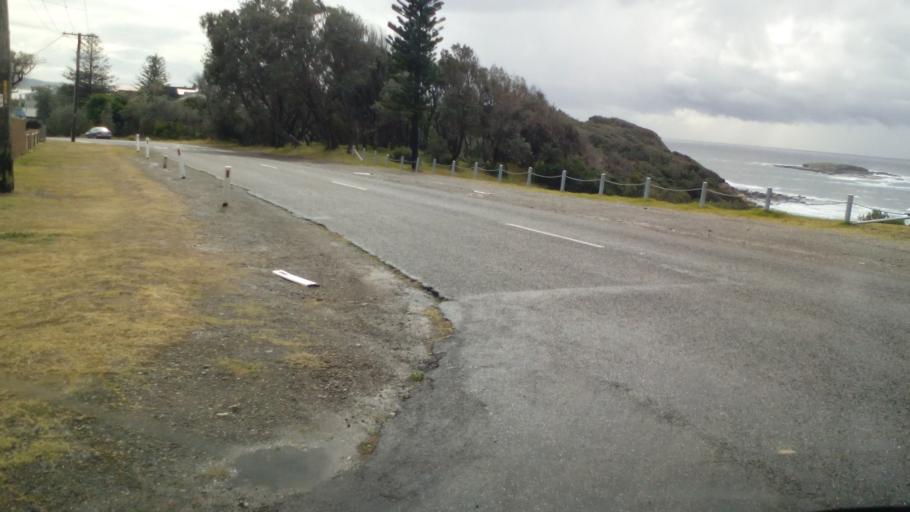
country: AU
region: New South Wales
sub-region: Lake Macquarie Shire
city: Belmont South
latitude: -33.0944
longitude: 151.6597
